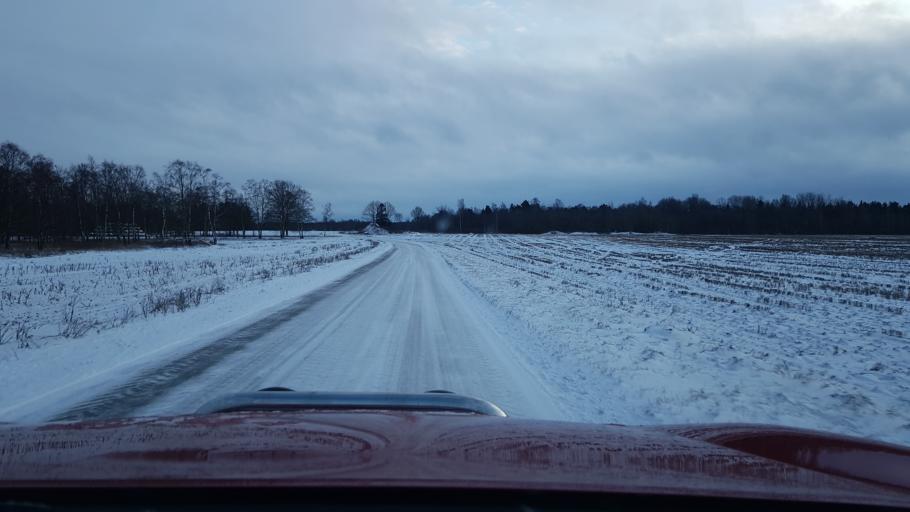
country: EE
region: Harju
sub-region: Maardu linn
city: Maardu
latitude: 59.4232
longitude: 25.0219
